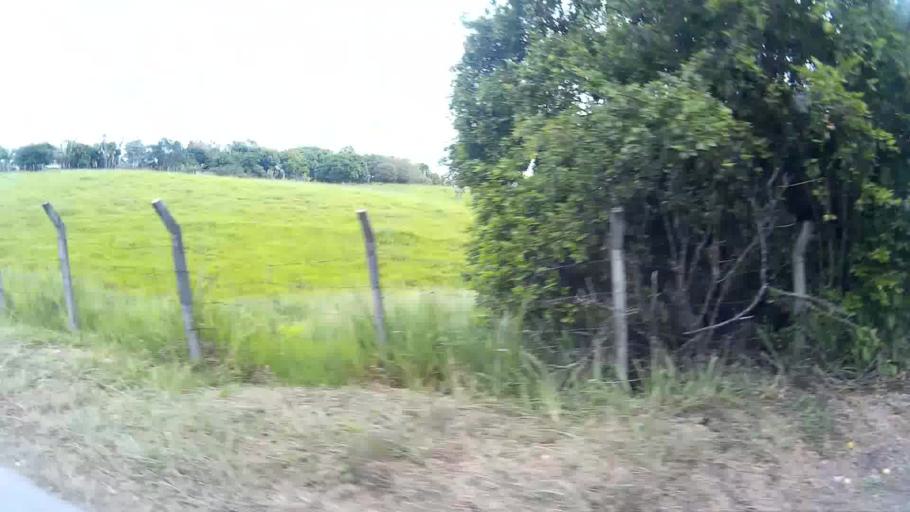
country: CO
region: Risaralda
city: La Virginia
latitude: 4.8266
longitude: -75.8429
